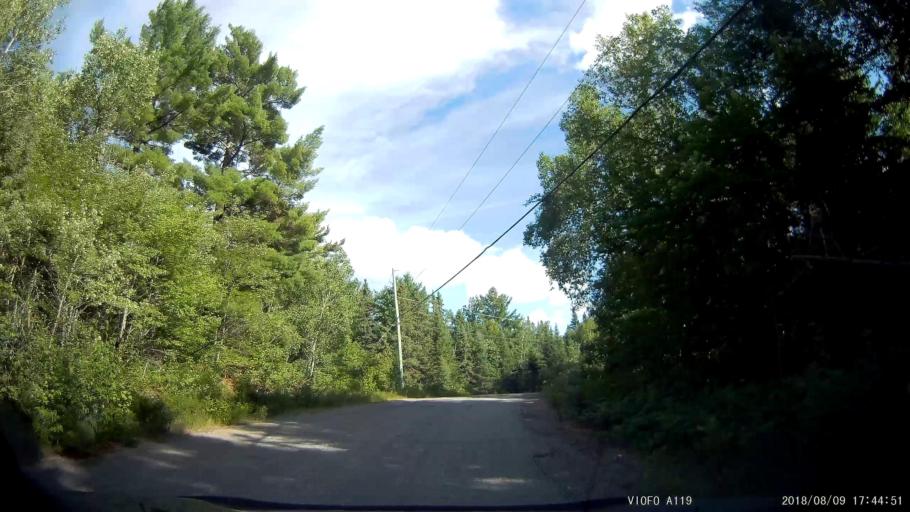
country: CA
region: Ontario
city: Rayside-Balfour
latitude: 46.6038
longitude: -81.5327
